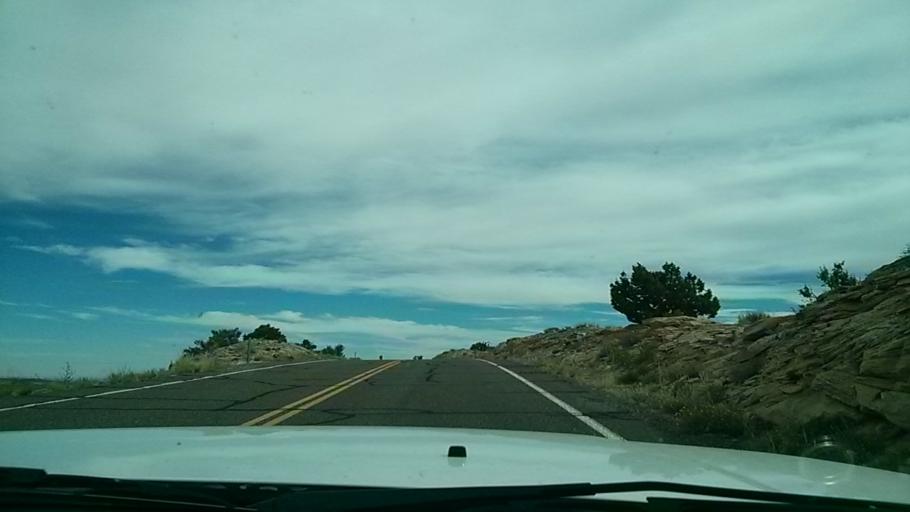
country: US
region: Utah
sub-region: Wayne County
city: Loa
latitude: 37.8331
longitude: -111.4159
